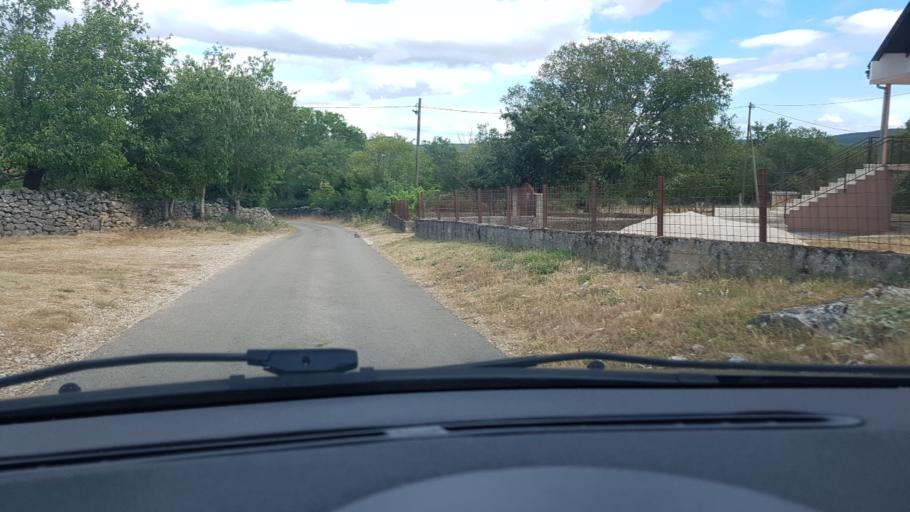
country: HR
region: Sibensko-Kniniska
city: Kistanje
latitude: 44.1100
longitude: 15.9258
